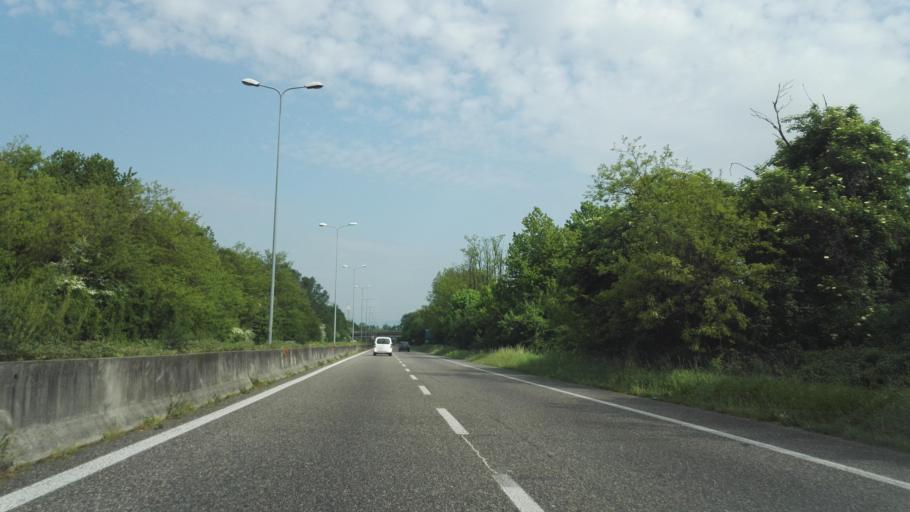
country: IT
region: Lombardy
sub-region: Provincia di Monza e Brianza
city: Seveso
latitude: 45.6454
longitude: 9.1559
